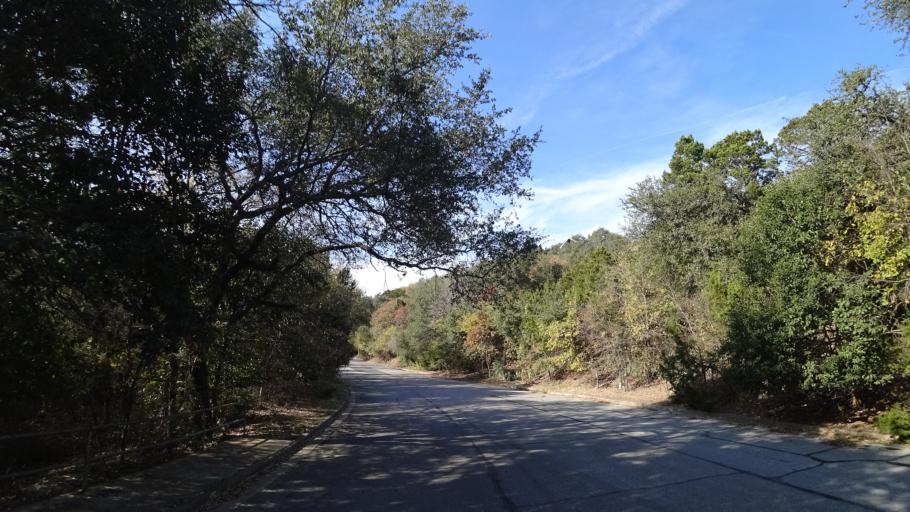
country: US
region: Texas
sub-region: Williamson County
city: Jollyville
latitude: 30.3832
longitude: -97.7559
